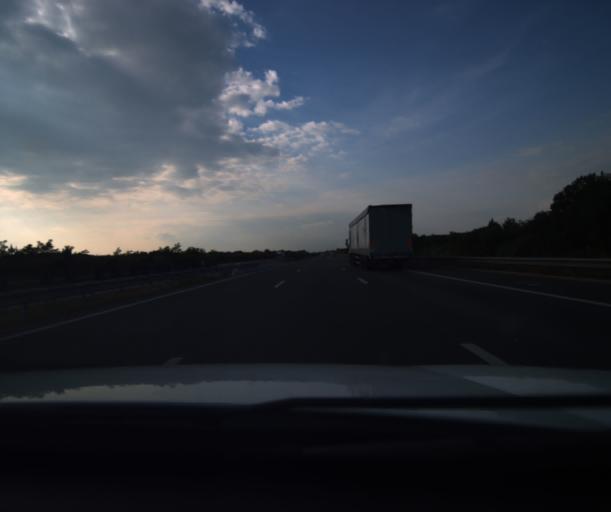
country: FR
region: Midi-Pyrenees
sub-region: Departement du Tarn-et-Garonne
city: Pompignan
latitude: 43.8252
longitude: 1.3456
